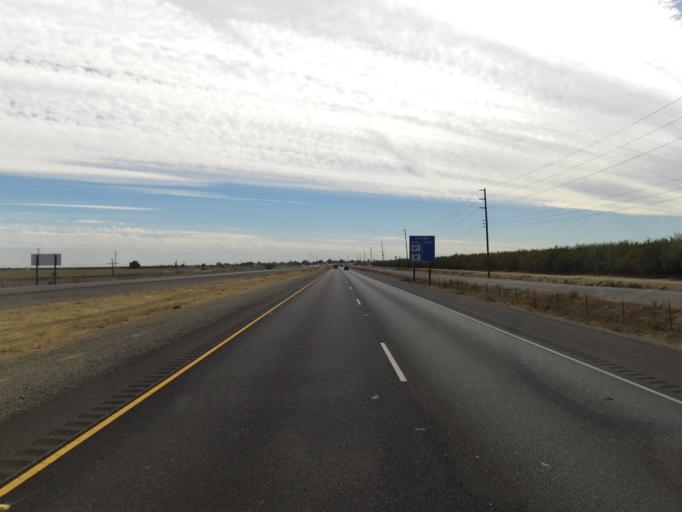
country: US
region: California
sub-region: Colusa County
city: Arbuckle
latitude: 39.0349
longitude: -122.0691
